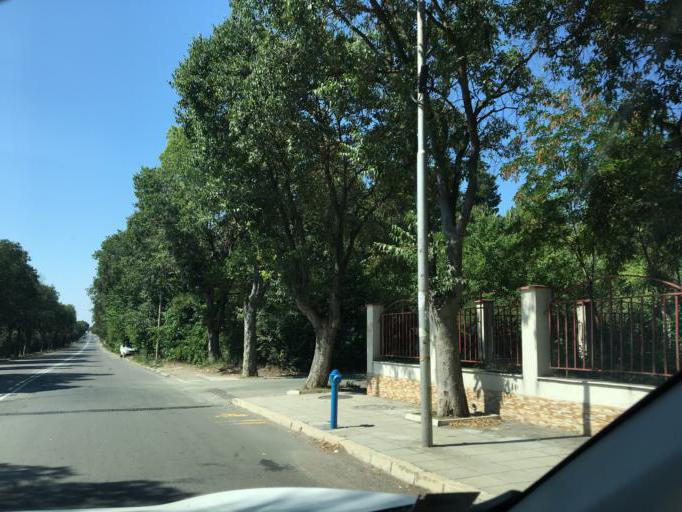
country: BG
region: Burgas
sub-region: Obshtina Kameno
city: Kameno
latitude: 42.6099
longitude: 27.3918
